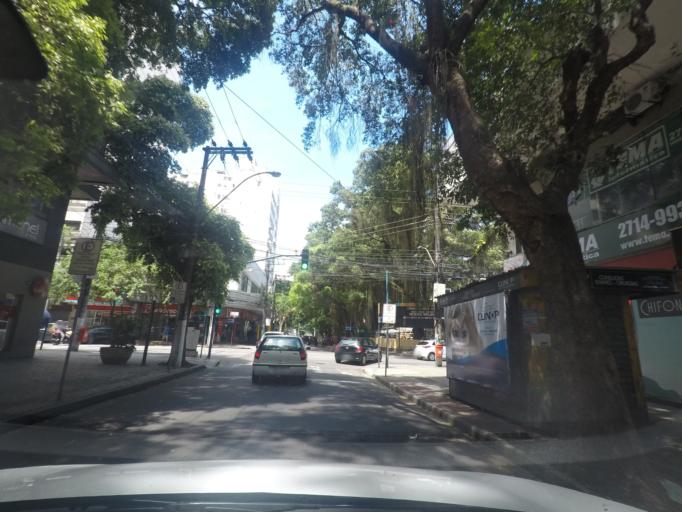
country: BR
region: Rio de Janeiro
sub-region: Niteroi
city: Niteroi
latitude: -22.9046
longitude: -43.1102
